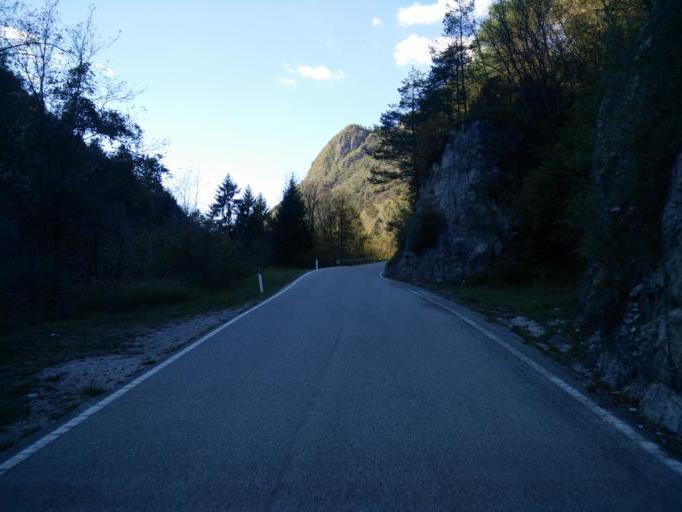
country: IT
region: Lombardy
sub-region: Provincia di Brescia
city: Valvestino
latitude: 45.7489
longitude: 10.5855
